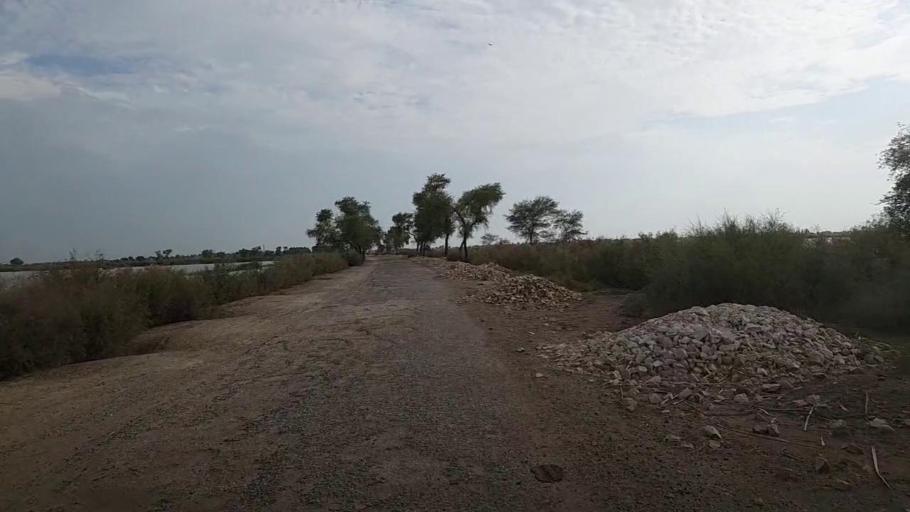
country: PK
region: Sindh
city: Thul
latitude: 28.2787
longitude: 68.8553
